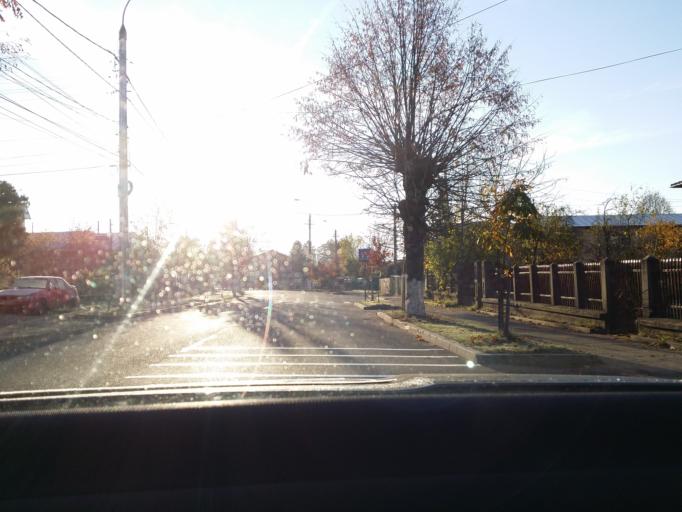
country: RO
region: Prahova
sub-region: Municipiul Campina
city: Campina
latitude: 45.1353
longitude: 25.7284
